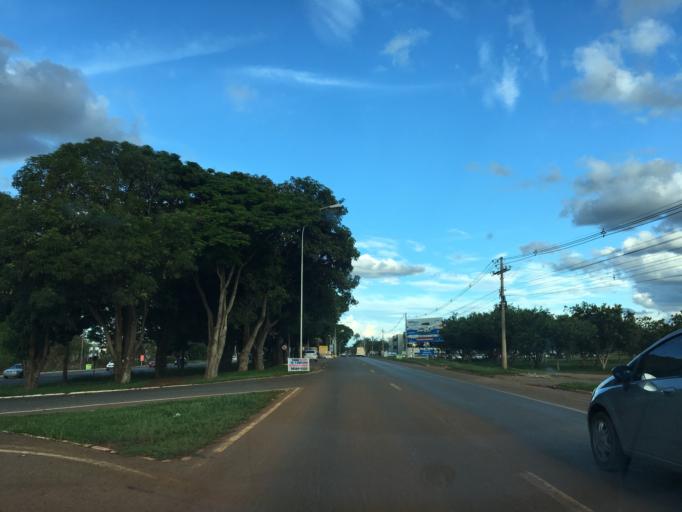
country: BR
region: Federal District
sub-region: Brasilia
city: Brasilia
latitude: -15.8591
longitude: -47.9299
